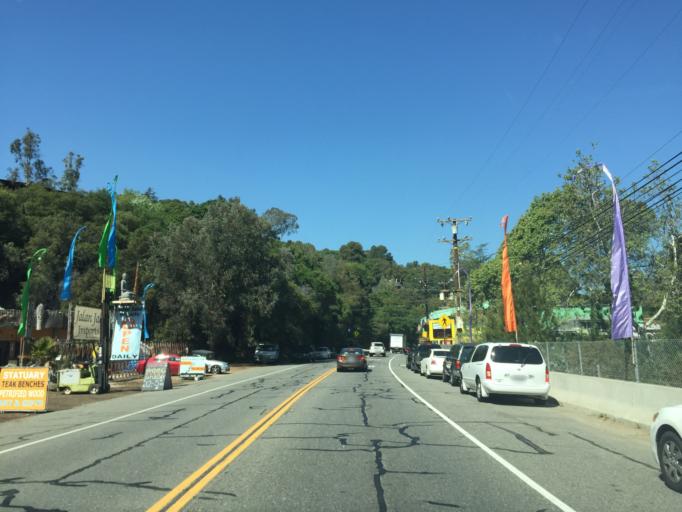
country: US
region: California
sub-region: Los Angeles County
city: Topanga
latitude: 34.0815
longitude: -118.5974
